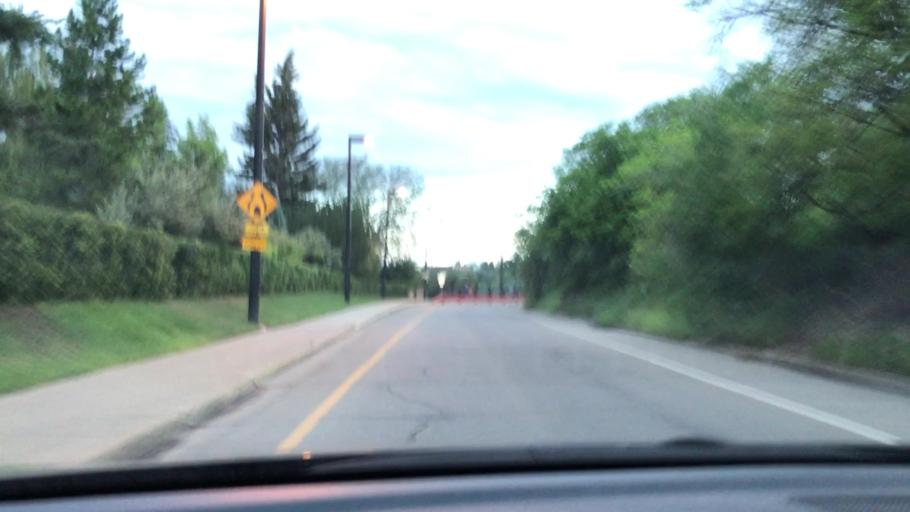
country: CA
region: Alberta
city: Edmonton
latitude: 53.5333
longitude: -113.5091
